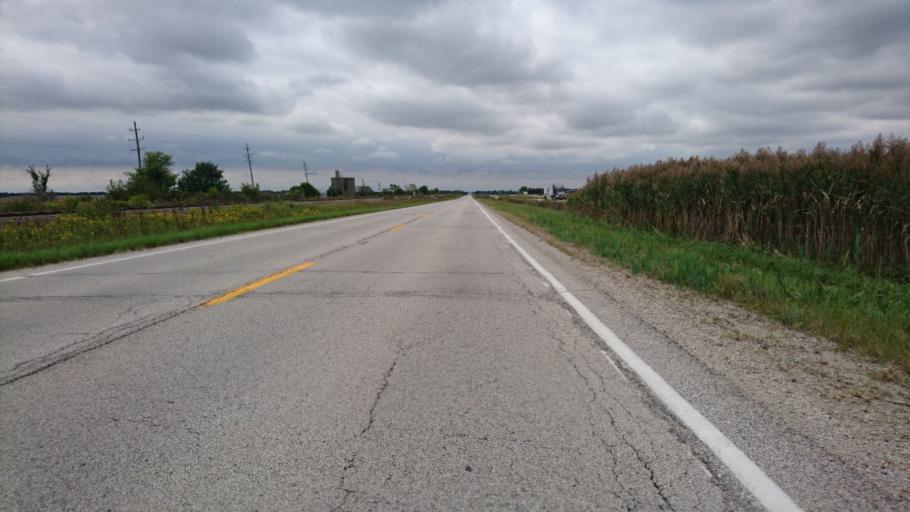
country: US
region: Illinois
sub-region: Livingston County
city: Odell
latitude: 40.9610
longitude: -88.5648
